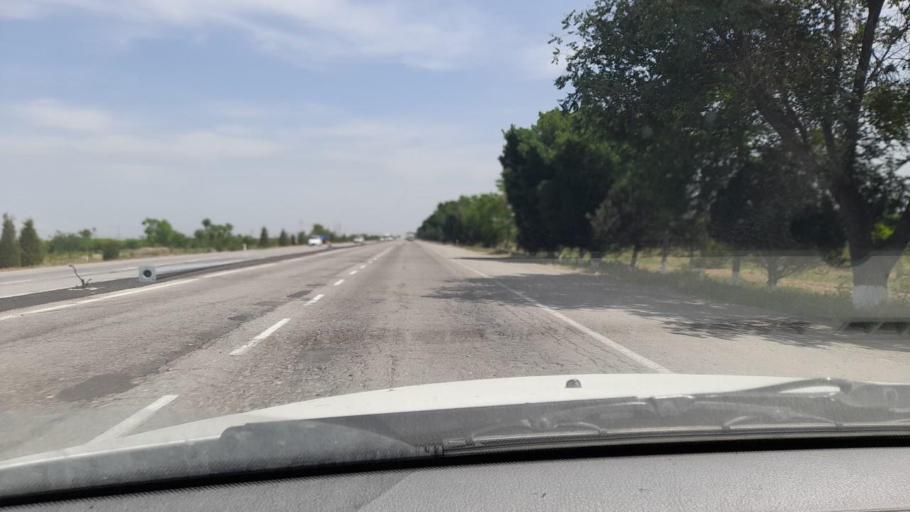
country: UZ
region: Navoiy
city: Beshrabot
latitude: 40.1300
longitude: 65.2015
